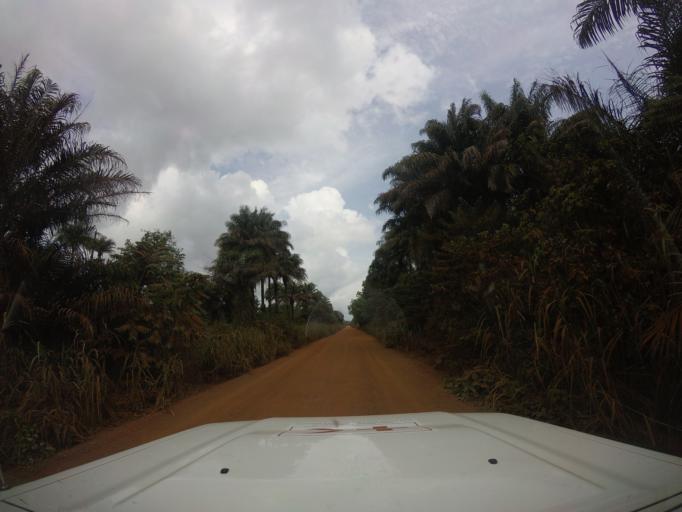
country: LR
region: Grand Cape Mount
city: Robertsport
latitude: 6.6845
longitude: -11.2436
